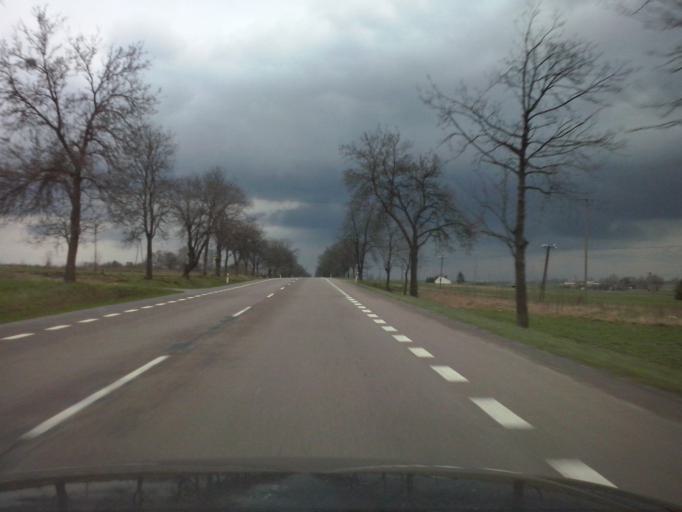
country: PL
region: Lublin Voivodeship
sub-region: Powiat chelmski
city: Rejowiec Fabryczny
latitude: 51.1761
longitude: 23.2415
